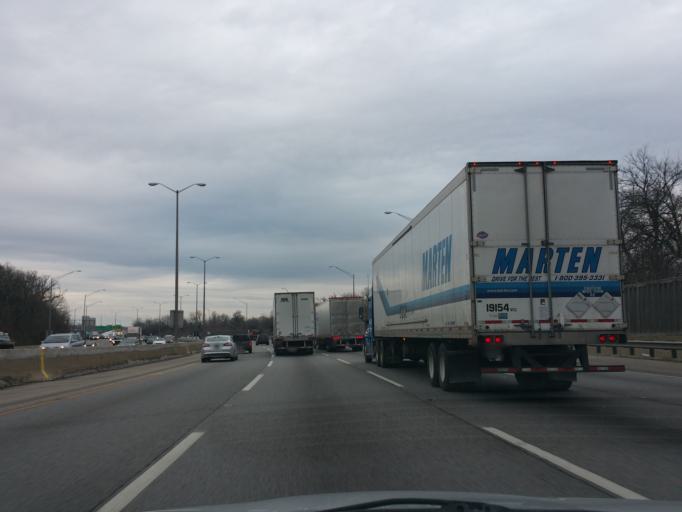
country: US
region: Illinois
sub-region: DuPage County
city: Oak Brook
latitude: 41.8275
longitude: -87.9184
